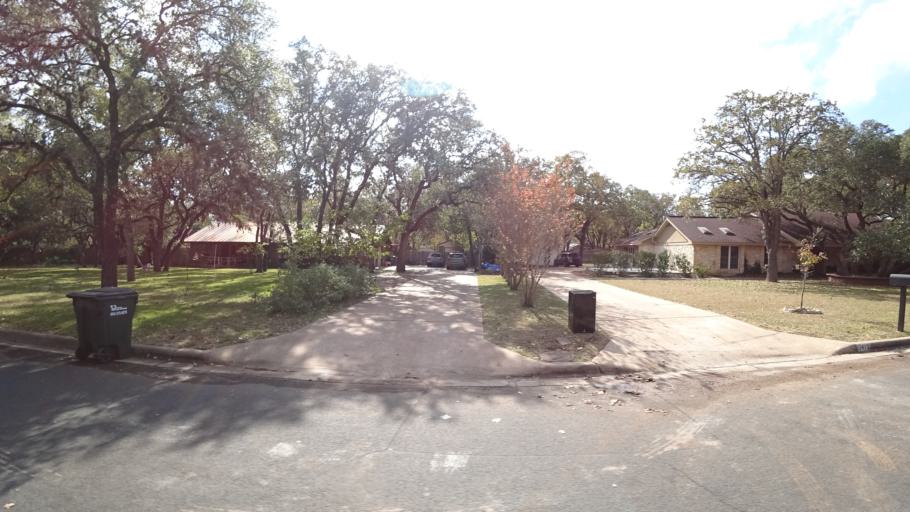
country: US
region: Texas
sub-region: Travis County
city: Shady Hollow
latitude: 30.1705
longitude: -97.8571
